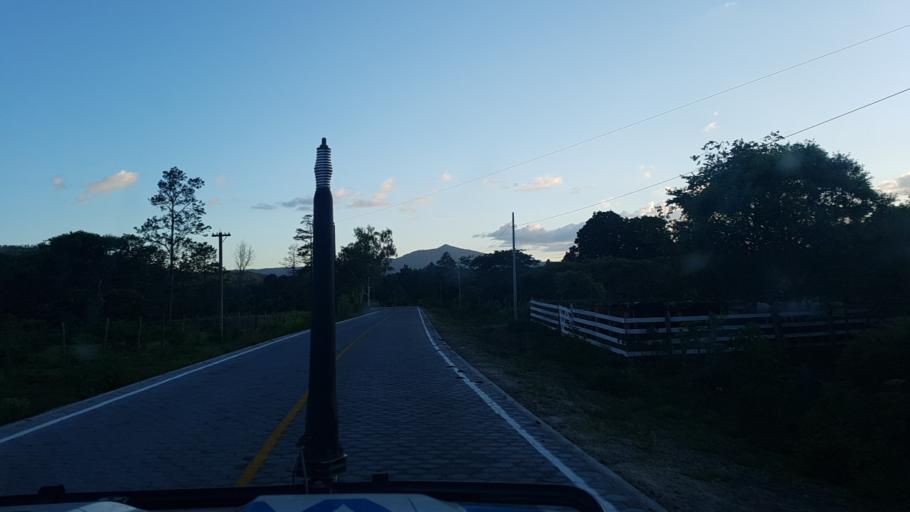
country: HN
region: El Paraiso
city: Santa Cruz
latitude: 13.7202
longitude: -86.6226
